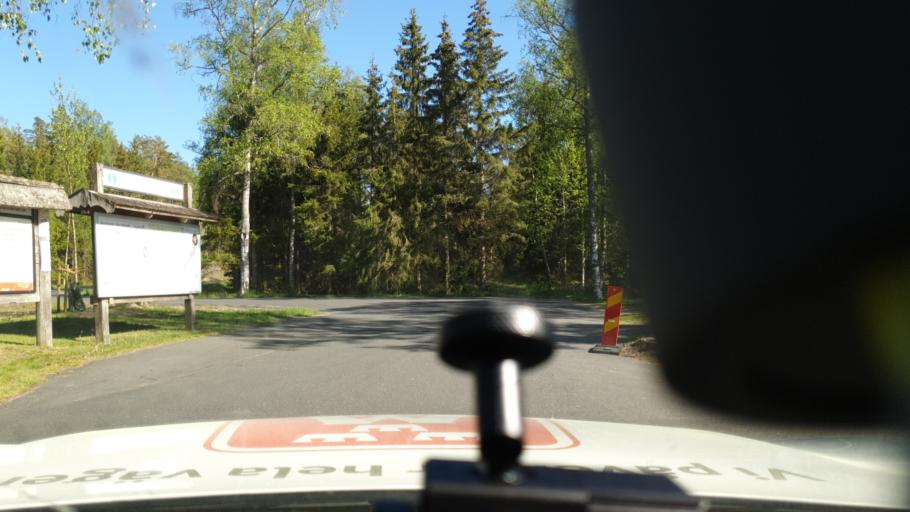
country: SE
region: Kronoberg
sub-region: Vaxjo Kommun
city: Braas
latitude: 57.2363
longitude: 15.1447
